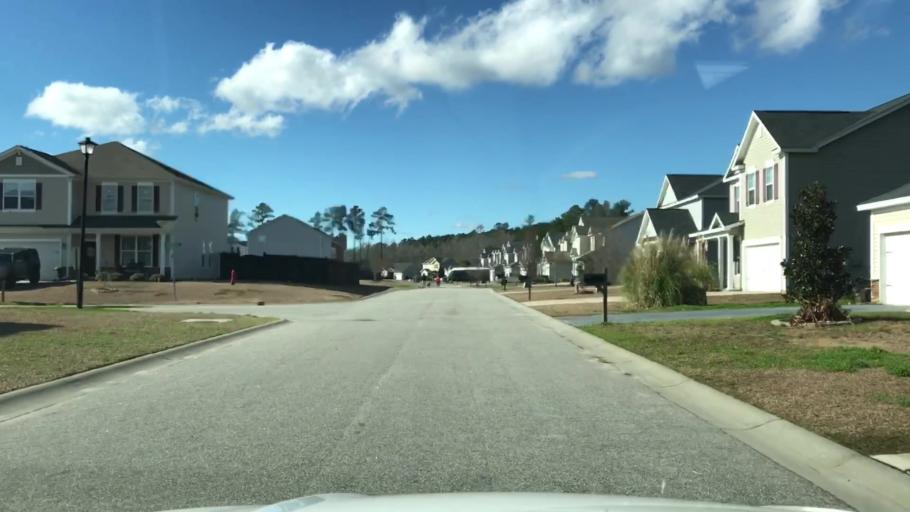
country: US
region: South Carolina
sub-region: Dorchester County
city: Summerville
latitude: 33.0903
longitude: -80.1941
